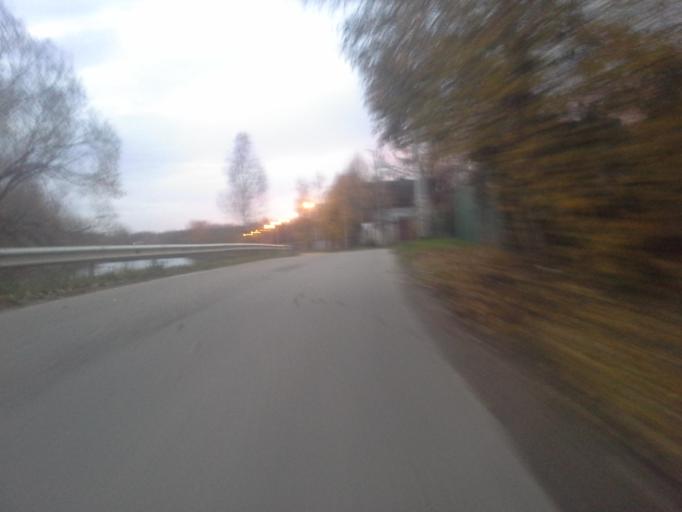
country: RU
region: Moskovskaya
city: Lesnoy Gorodok
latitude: 55.6310
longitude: 37.2229
